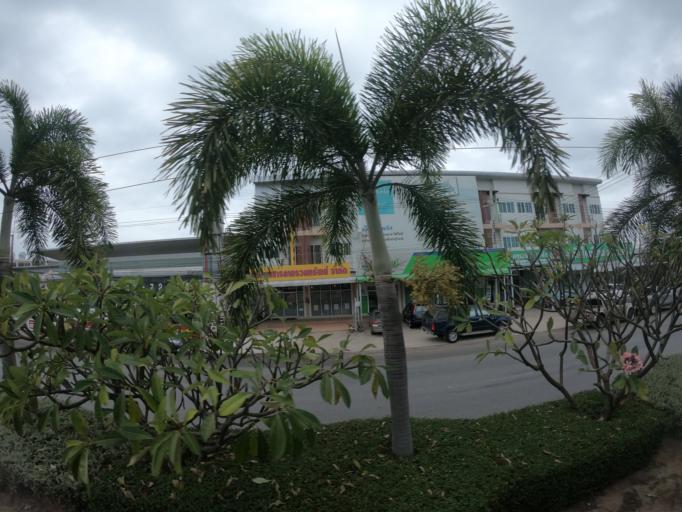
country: TH
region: Maha Sarakham
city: Maha Sarakham
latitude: 16.1783
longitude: 103.2977
